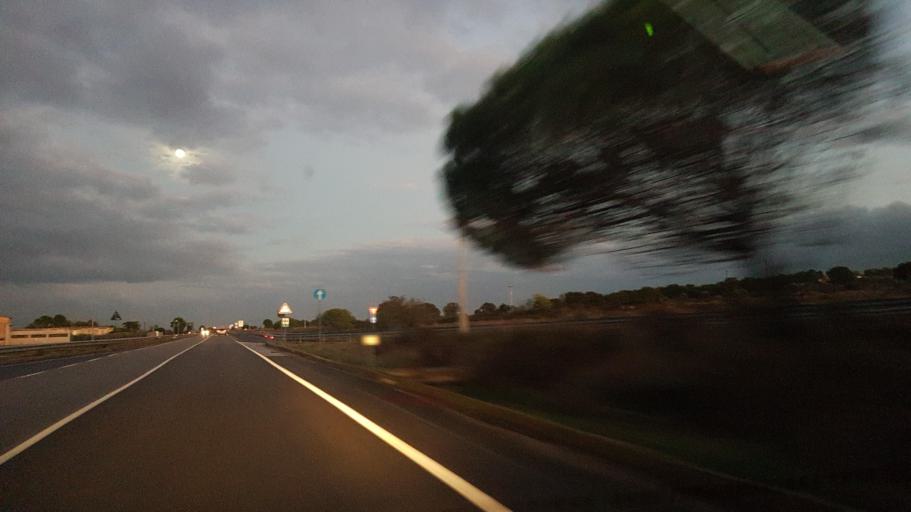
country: IT
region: Apulia
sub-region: Provincia di Taranto
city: Laterza
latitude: 40.6490
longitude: 16.8239
